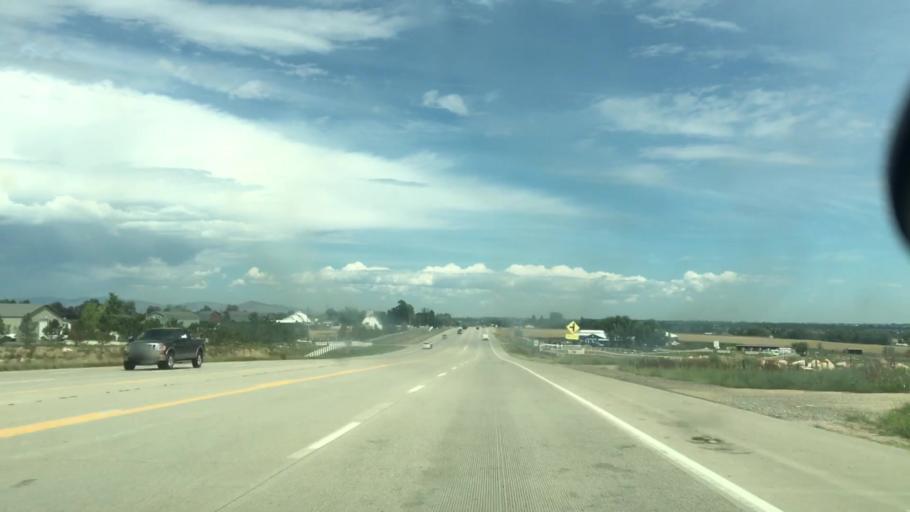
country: US
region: Colorado
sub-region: Larimer County
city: Berthoud
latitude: 40.2604
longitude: -105.1025
